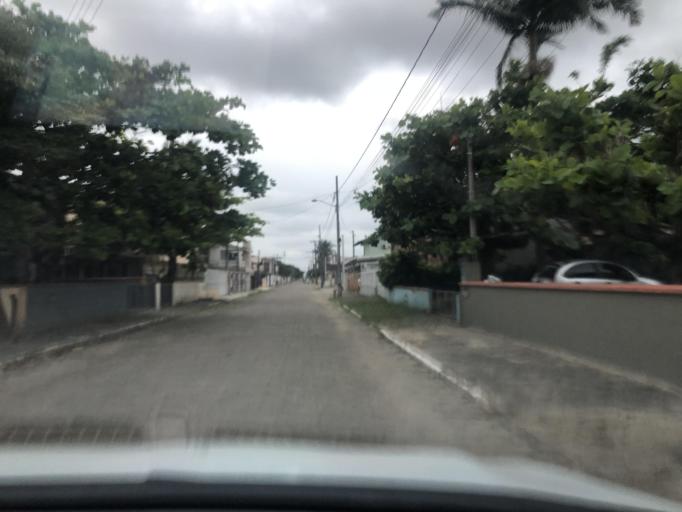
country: BR
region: Santa Catarina
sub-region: Sao Francisco Do Sul
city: Sao Francisco do Sul
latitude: -26.2268
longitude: -48.5135
